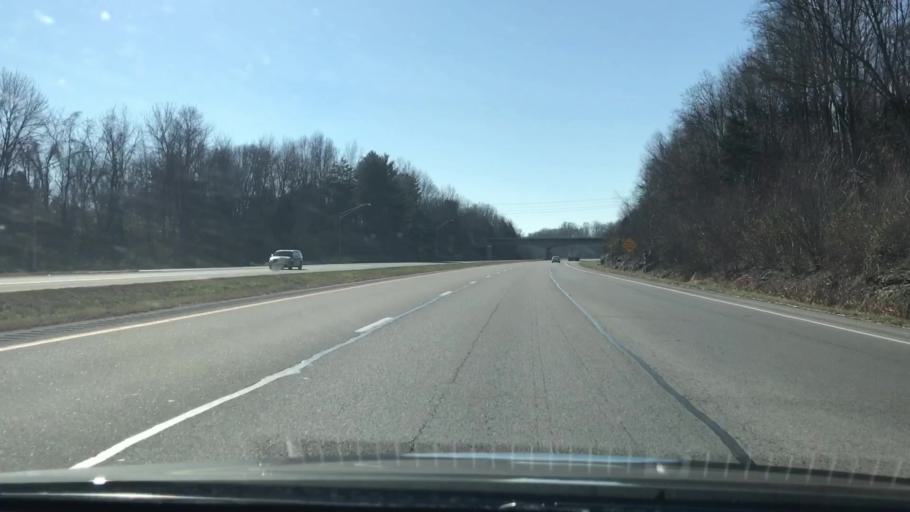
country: US
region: Kentucky
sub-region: Barren County
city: Glasgow
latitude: 36.9826
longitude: -85.8992
